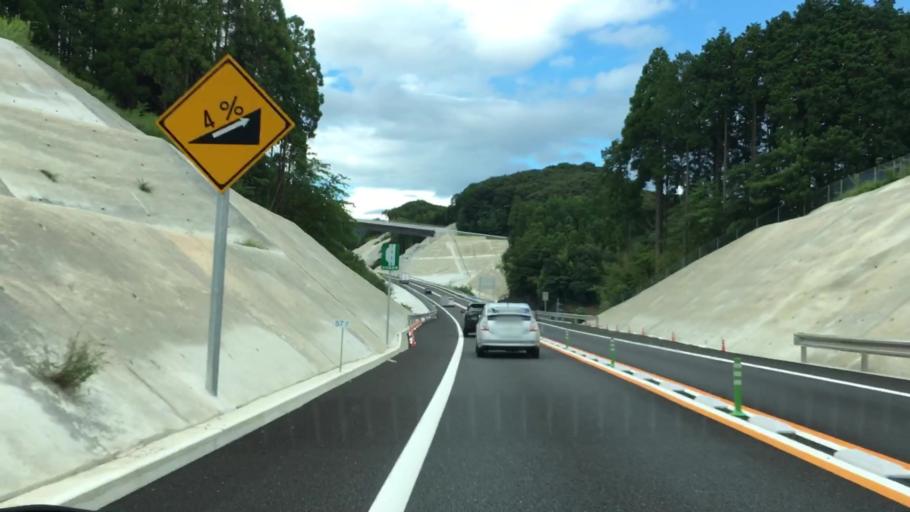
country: JP
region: Saga Prefecture
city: Imaricho-ko
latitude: 33.3008
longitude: 129.9150
